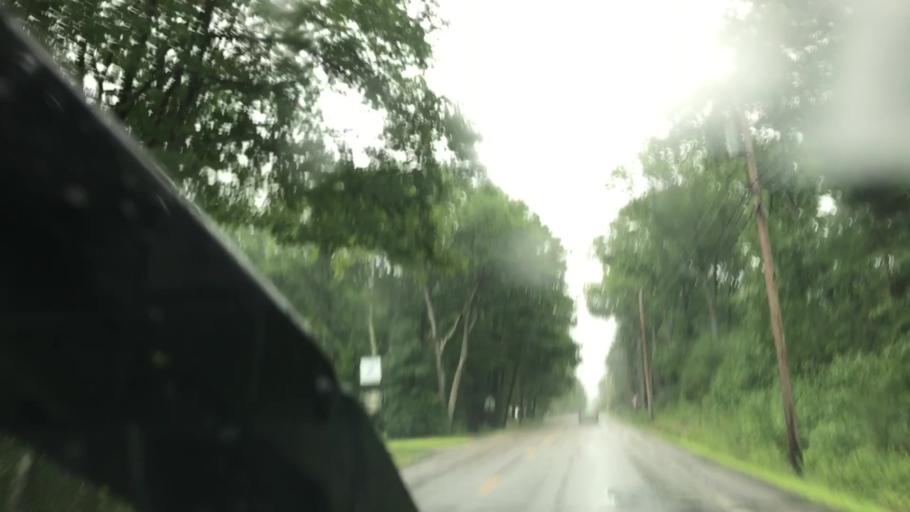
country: US
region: New Hampshire
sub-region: Strafford County
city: Rollinsford
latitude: 43.2848
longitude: -70.8171
